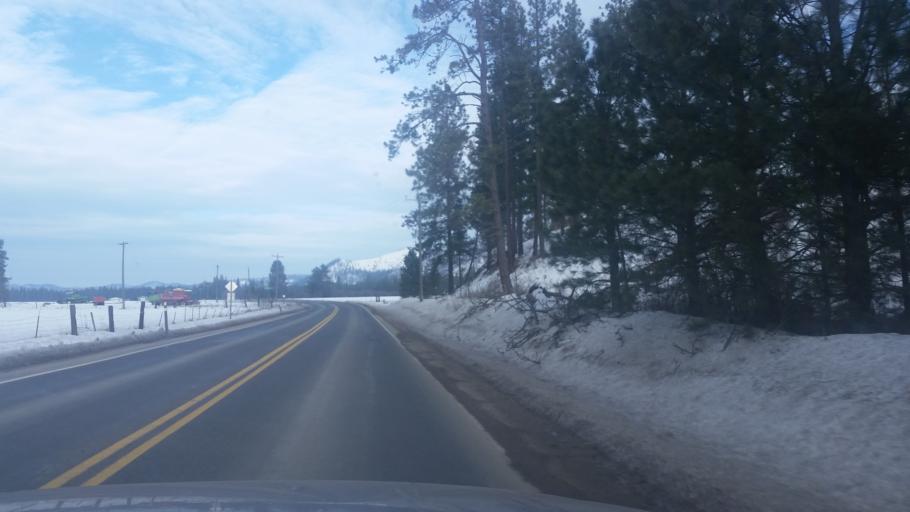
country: US
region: Washington
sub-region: Spokane County
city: Deer Park
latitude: 47.9397
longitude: -117.7697
